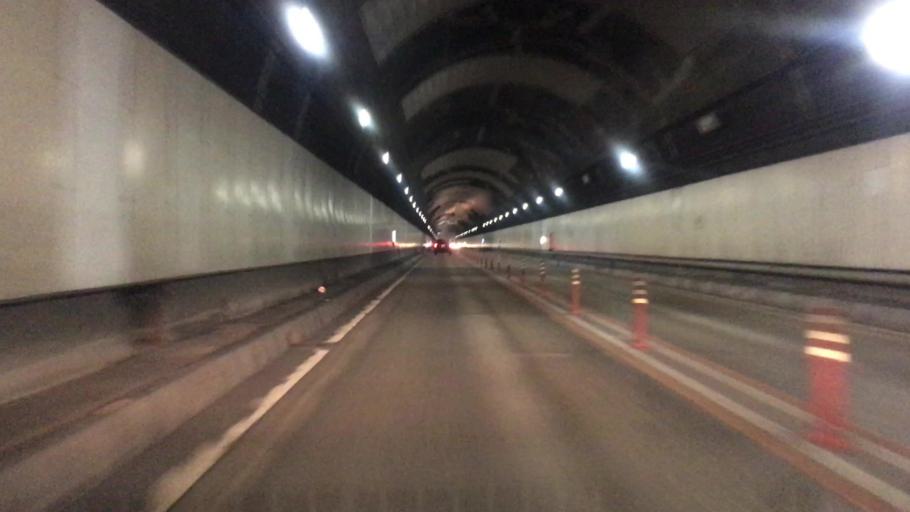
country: JP
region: Kyoto
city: Fukuchiyama
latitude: 35.2974
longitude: 134.9500
